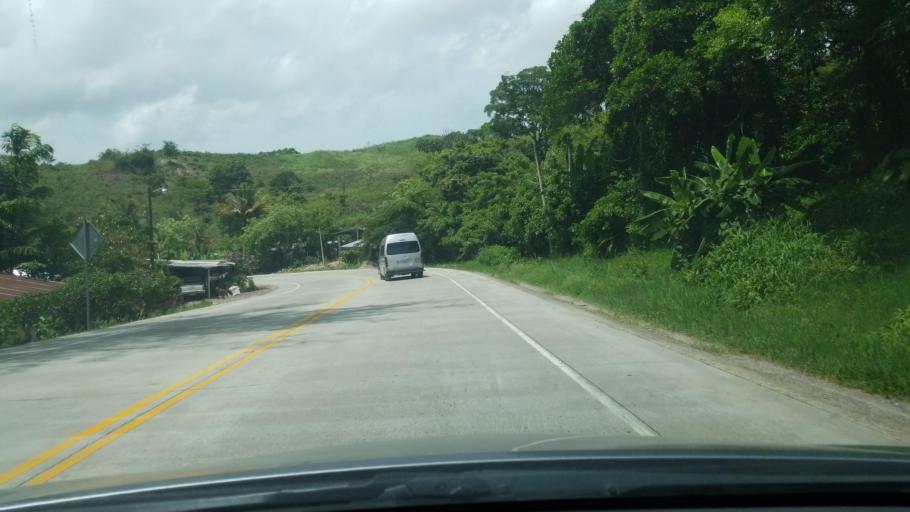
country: HN
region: Copan
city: San Juan de Planes
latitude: 14.9688
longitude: -88.7823
